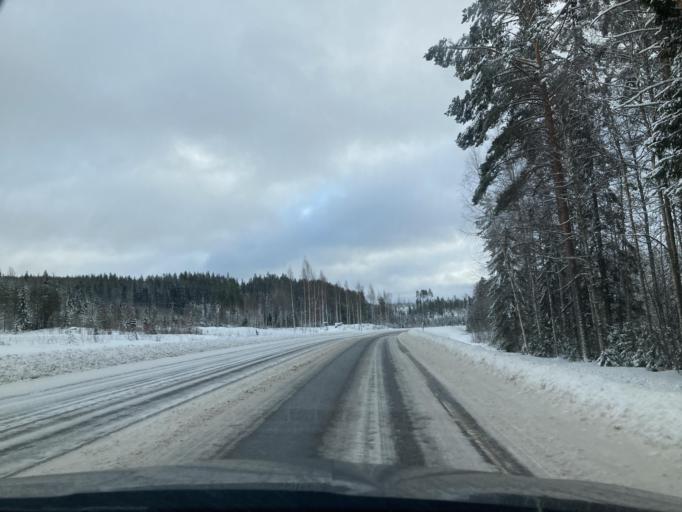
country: FI
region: Central Finland
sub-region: Jaemsae
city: Jaemsae
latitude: 61.7166
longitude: 25.2720
